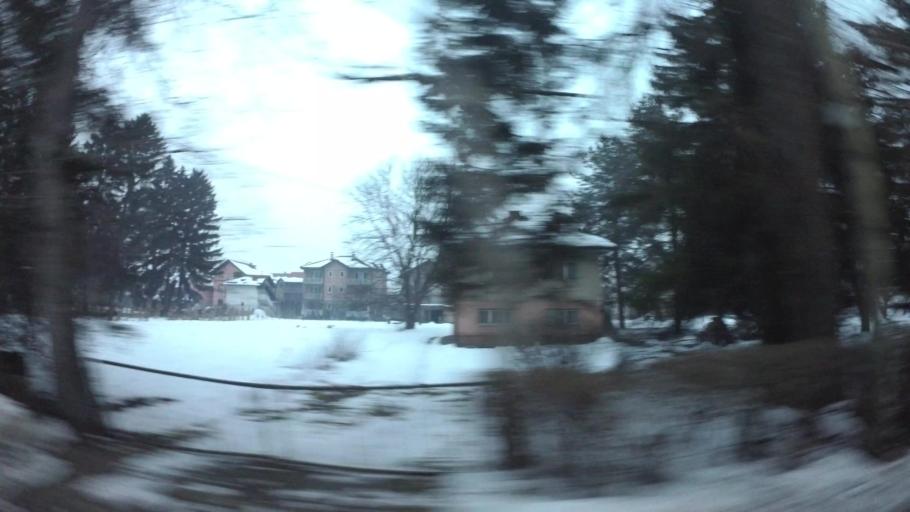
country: BA
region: Federation of Bosnia and Herzegovina
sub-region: Kanton Sarajevo
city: Sarajevo
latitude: 43.8506
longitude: 18.3049
